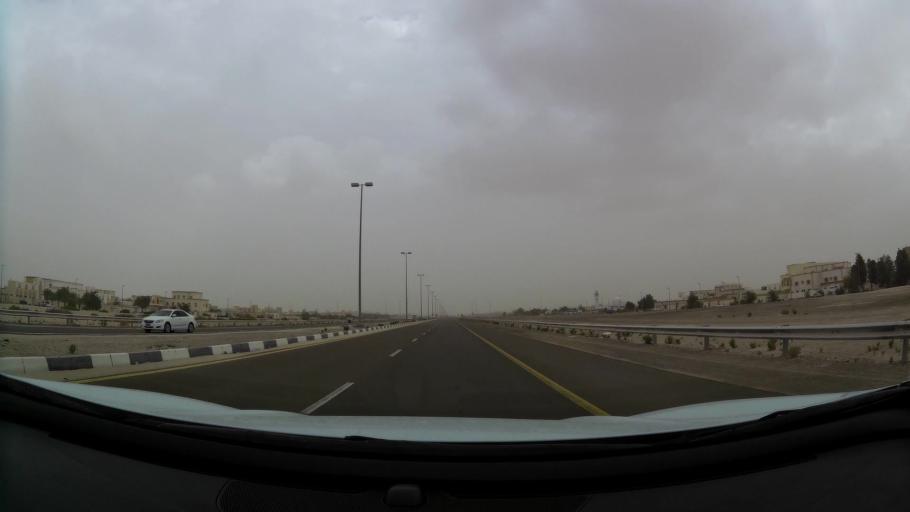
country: AE
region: Abu Dhabi
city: Abu Dhabi
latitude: 24.4014
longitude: 54.7208
